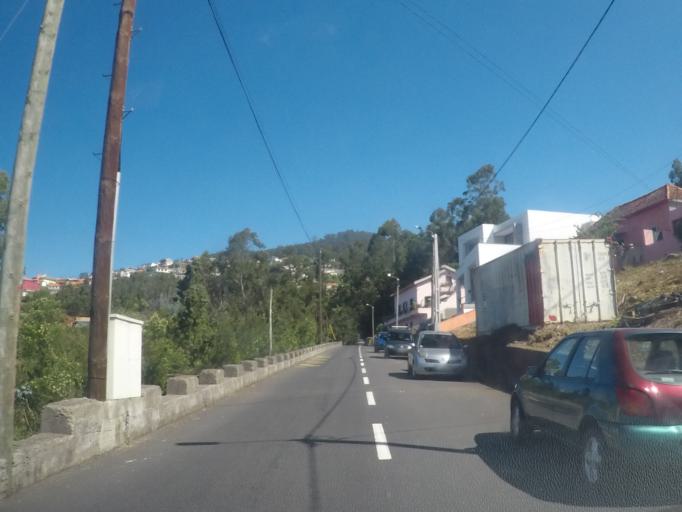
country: PT
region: Madeira
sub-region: Camara de Lobos
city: Curral das Freiras
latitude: 32.6782
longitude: -16.9664
